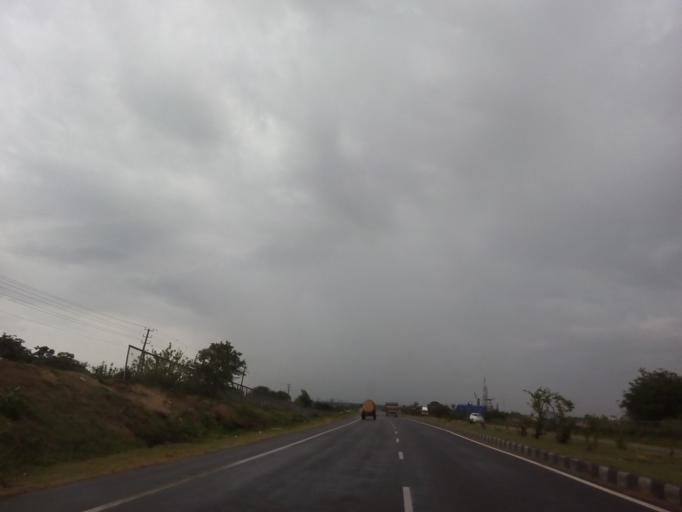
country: IN
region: Karnataka
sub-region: Davanagere
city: Harihar
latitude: 14.4303
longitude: 75.9315
